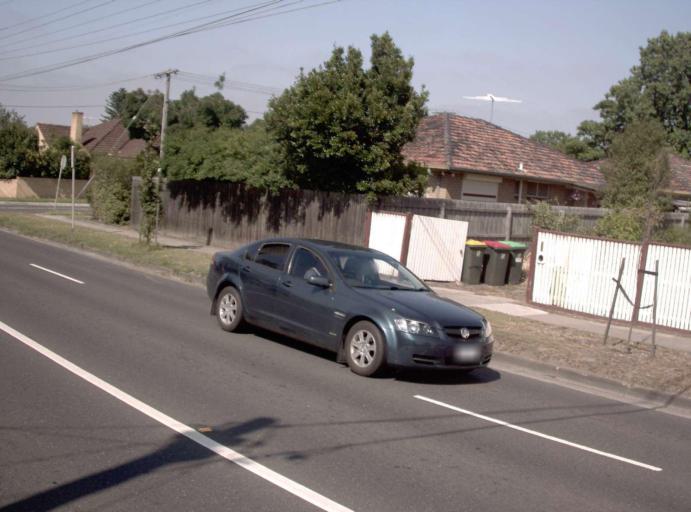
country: AU
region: Victoria
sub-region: Monash
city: Oakleigh South
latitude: -37.9269
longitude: 145.0819
